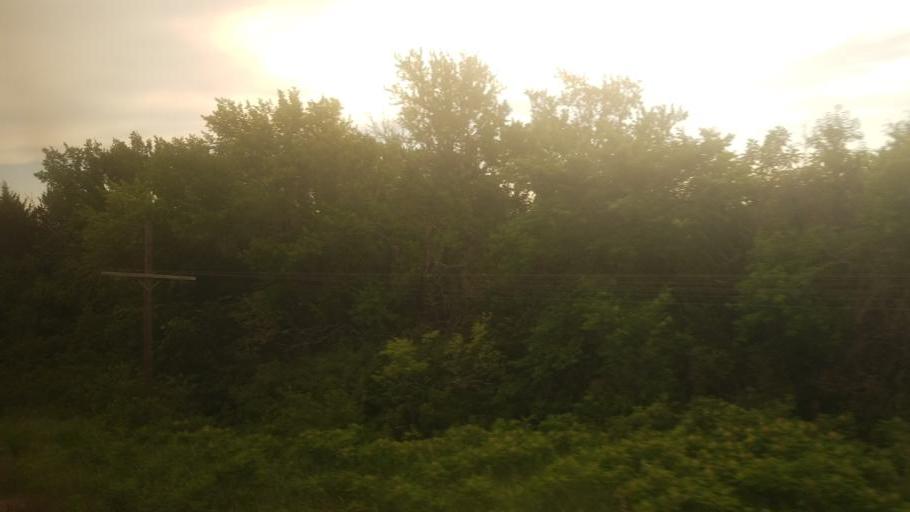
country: US
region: Kansas
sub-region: Osage County
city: Carbondale
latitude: 38.9331
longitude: -95.6889
